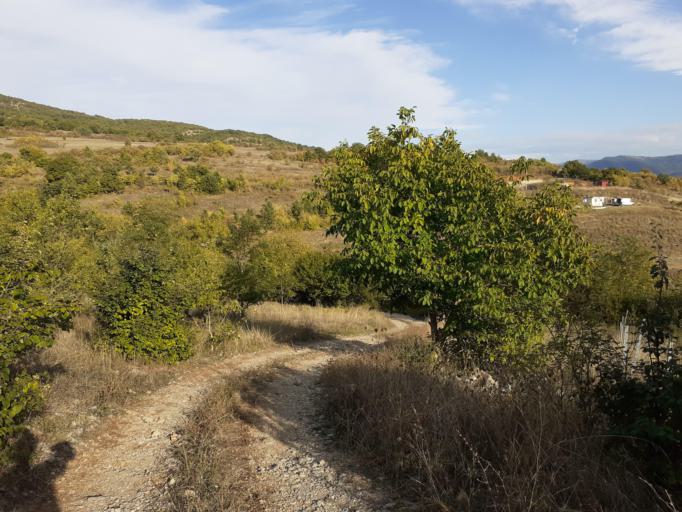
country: RS
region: Central Serbia
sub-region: Pirotski Okrug
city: Dimitrovgrad
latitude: 43.0232
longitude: 22.7924
